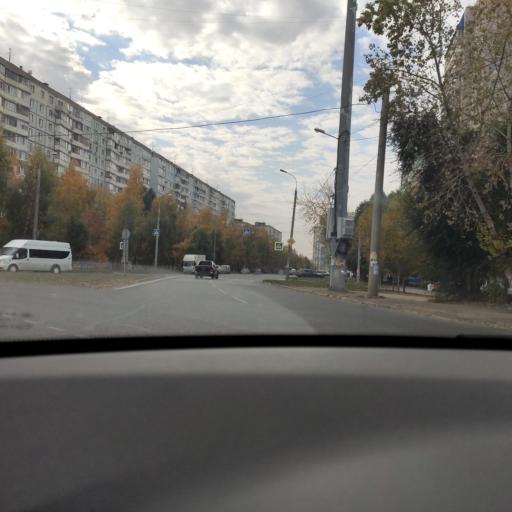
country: RU
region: Samara
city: Samara
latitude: 53.2593
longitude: 50.2241
